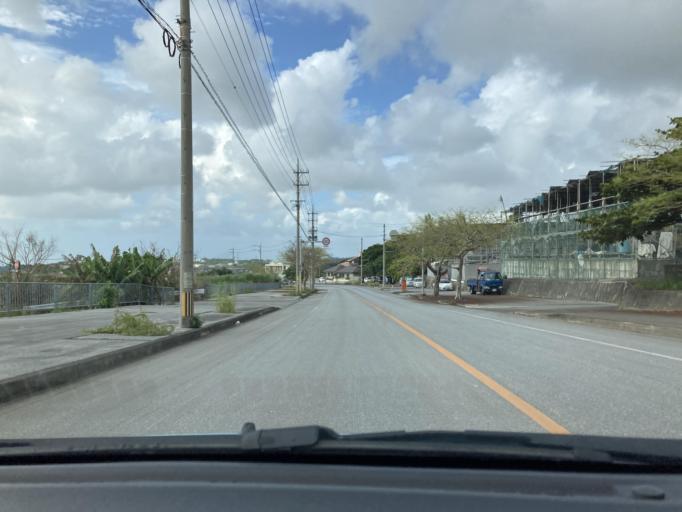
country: JP
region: Okinawa
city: Itoman
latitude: 26.1232
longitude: 127.6933
